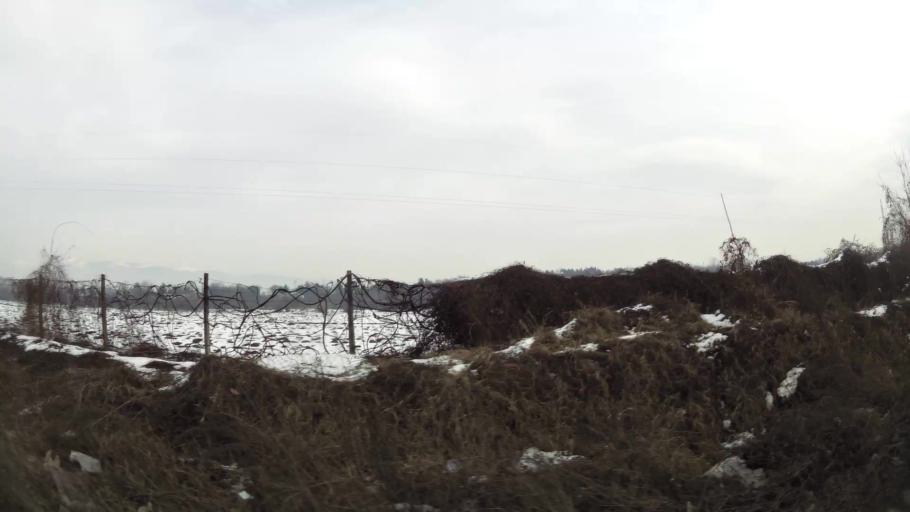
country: MK
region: Suto Orizari
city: Suto Orizare
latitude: 42.0209
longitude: 21.4099
